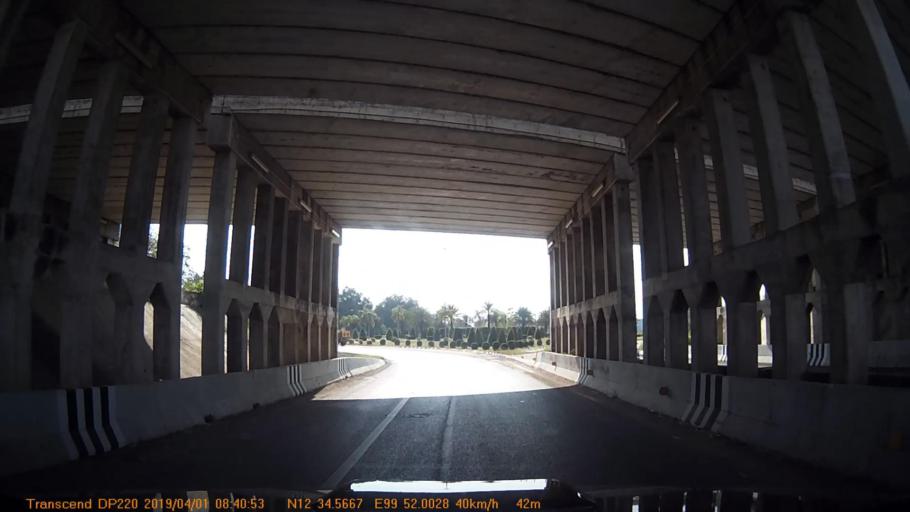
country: TH
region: Prachuap Khiri Khan
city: Hua Hin
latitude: 12.5757
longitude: 99.8668
